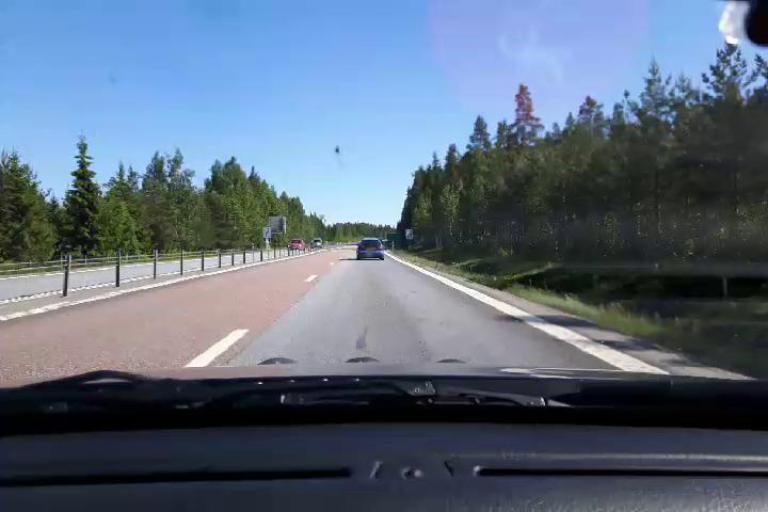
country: SE
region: Gaevleborg
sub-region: Gavle Kommun
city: Norrsundet
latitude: 60.8948
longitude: 17.0307
